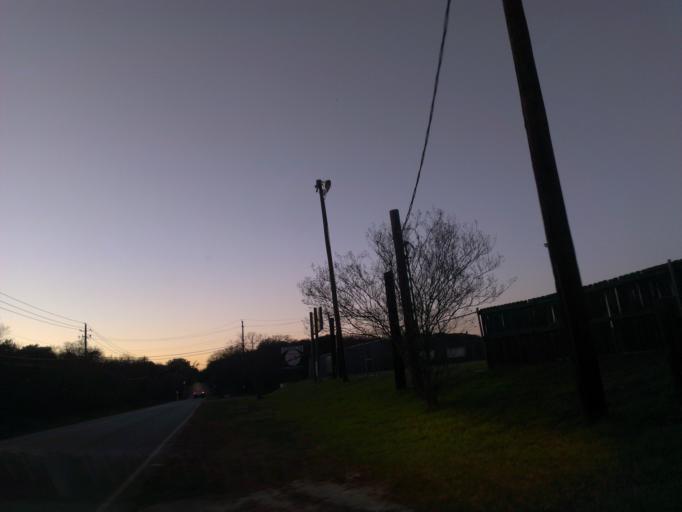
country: US
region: Texas
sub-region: Travis County
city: Wells Branch
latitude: 30.4184
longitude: -97.7092
